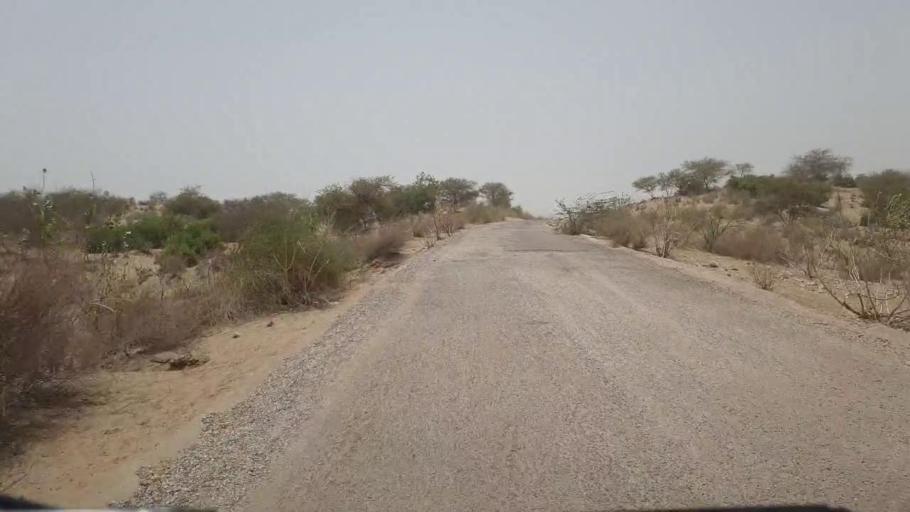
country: PK
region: Sindh
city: Naukot
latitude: 24.7691
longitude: 69.5379
